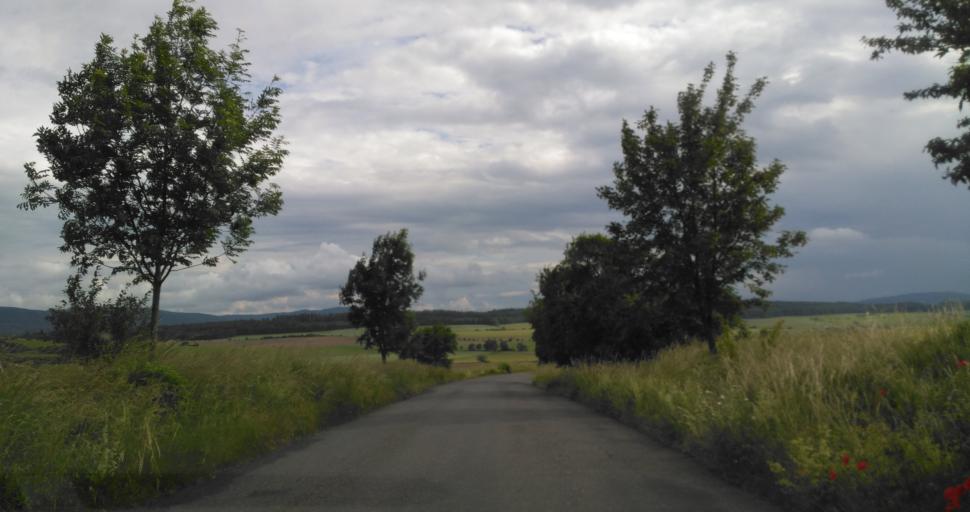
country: CZ
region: Central Bohemia
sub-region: Okres Beroun
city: Kraluv Dvur
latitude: 49.8910
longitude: 14.0747
